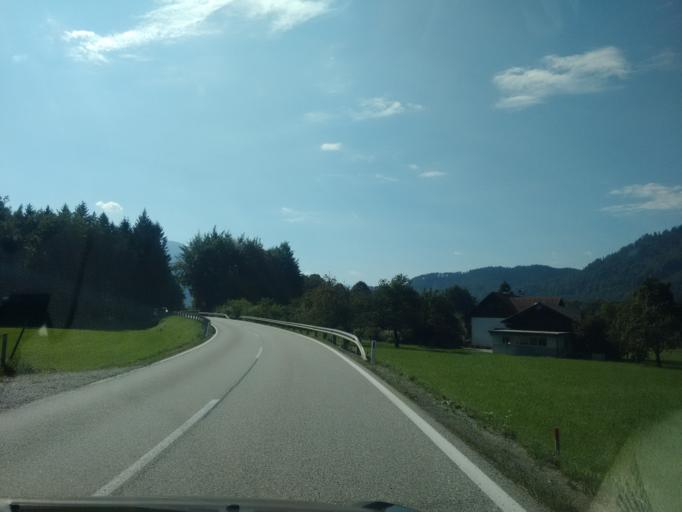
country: AT
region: Upper Austria
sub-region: Politischer Bezirk Gmunden
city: Gruenau im Almtal
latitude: 47.8745
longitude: 13.9426
